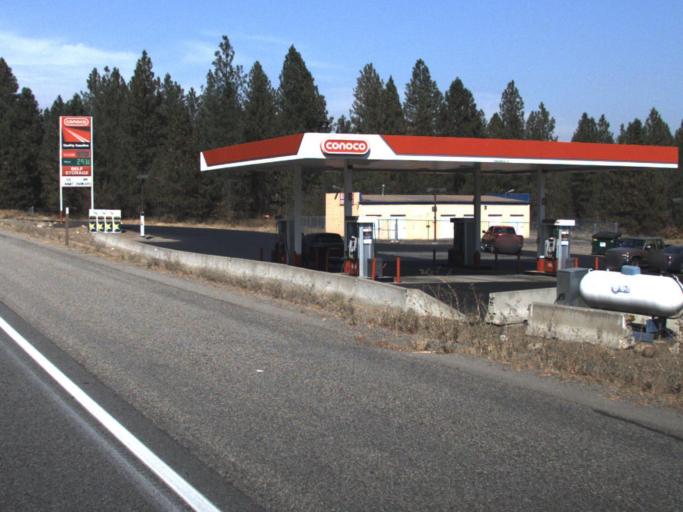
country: US
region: Washington
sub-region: Spokane County
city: Deer Park
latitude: 47.9146
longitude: -117.3502
